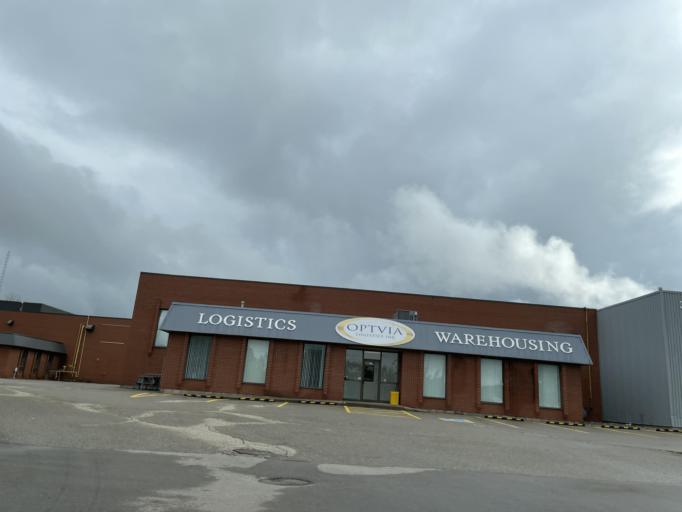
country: CA
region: Ontario
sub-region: Wellington County
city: Guelph
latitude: 43.5475
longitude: -80.3014
